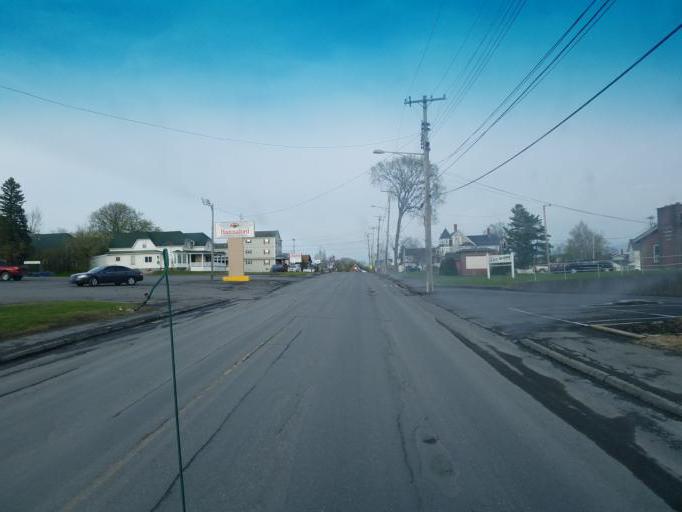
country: US
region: Maine
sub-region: Aroostook County
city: Caribou
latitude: 46.8606
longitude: -68.0091
